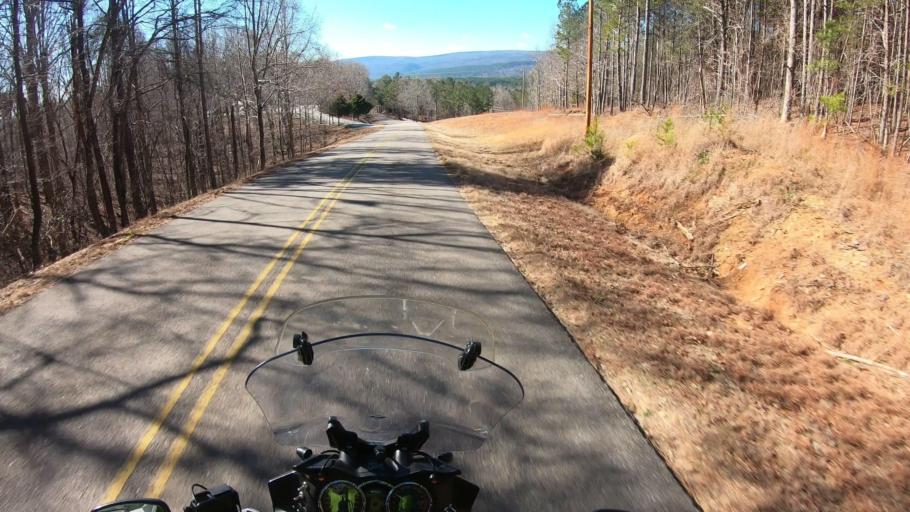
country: US
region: Alabama
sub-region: Clay County
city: Lineville
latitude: 33.4522
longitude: -85.7573
